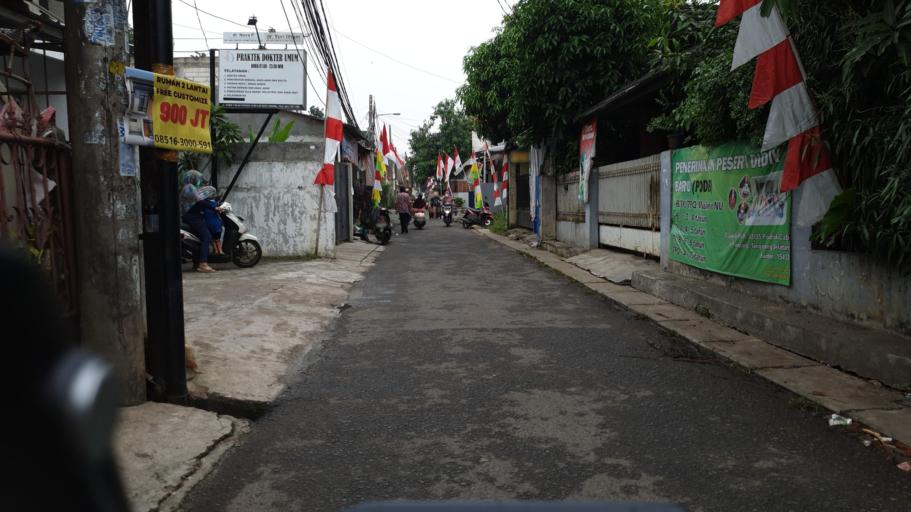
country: ID
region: West Java
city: Pamulang
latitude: -6.3326
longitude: 106.7697
